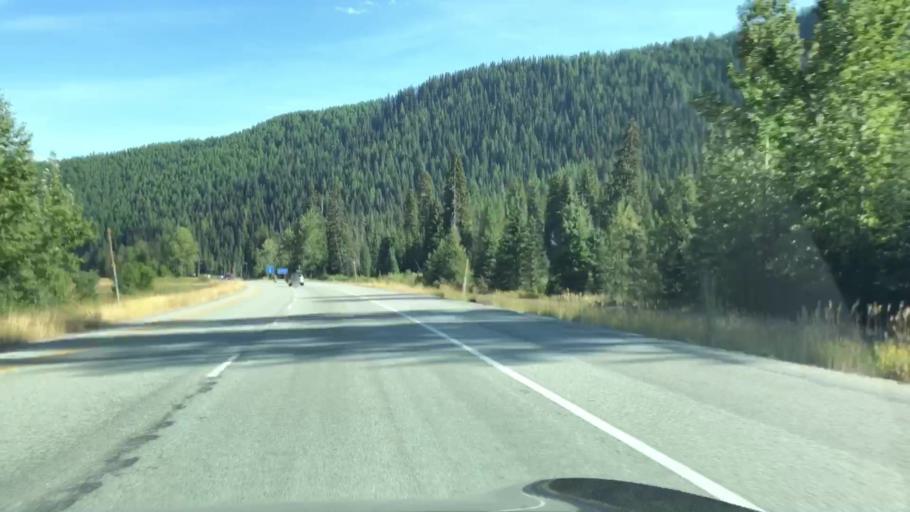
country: US
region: Idaho
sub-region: Shoshone County
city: Wallace
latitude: 47.4234
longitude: -115.6357
